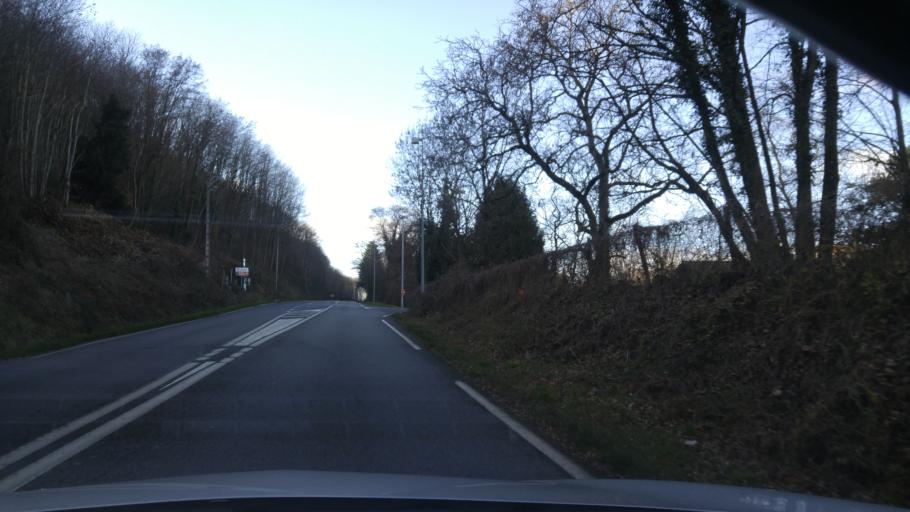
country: FR
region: Rhone-Alpes
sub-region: Departement de l'Isere
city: Villefontaine
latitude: 45.6030
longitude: 5.1569
